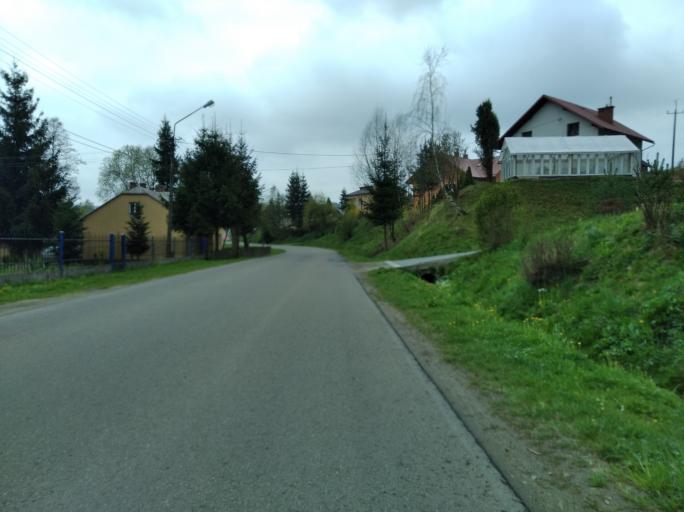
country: PL
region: Subcarpathian Voivodeship
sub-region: Powiat brzozowski
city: Jablonka
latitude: 49.7391
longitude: 22.0791
